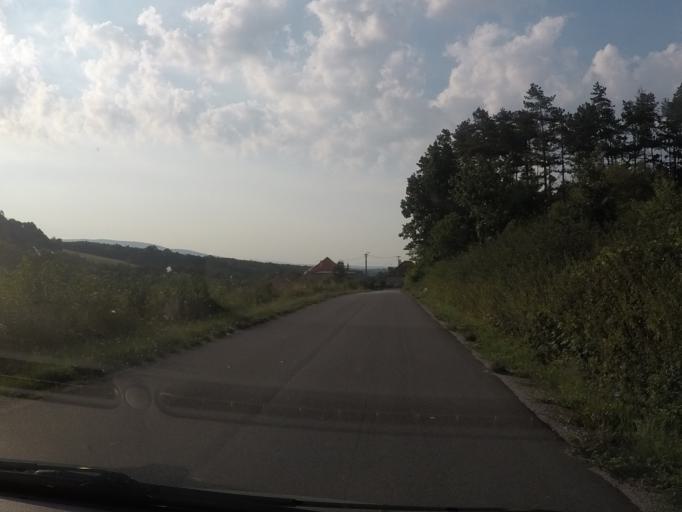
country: SK
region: Nitriansky
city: Zlate Moravce
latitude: 48.4341
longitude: 18.3231
